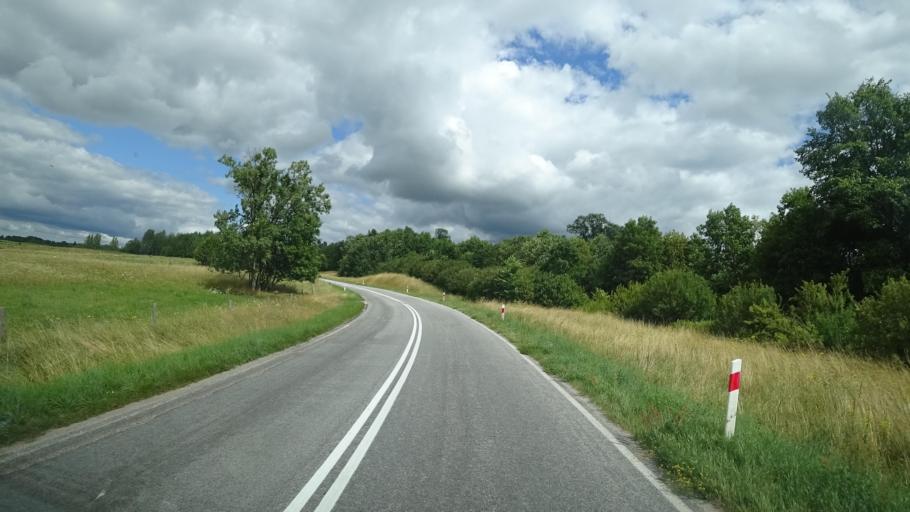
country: PL
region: Warmian-Masurian Voivodeship
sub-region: Powiat goldapski
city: Goldap
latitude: 54.2078
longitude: 22.1992
